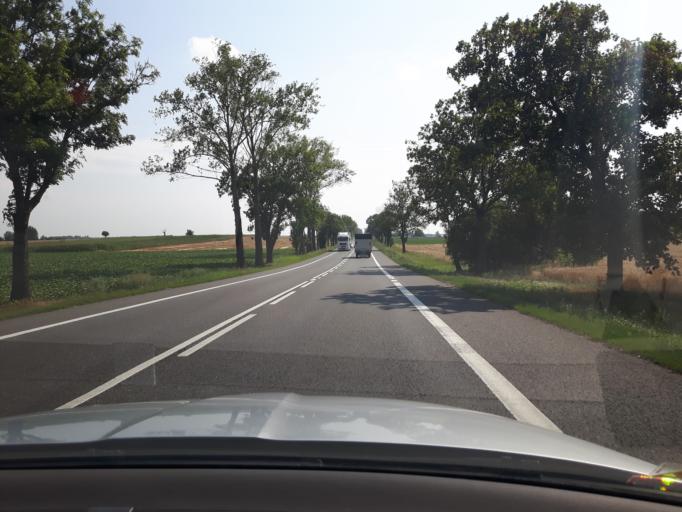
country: PL
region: Masovian Voivodeship
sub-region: Powiat mlawski
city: Wisniewo
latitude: 53.0541
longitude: 20.3449
